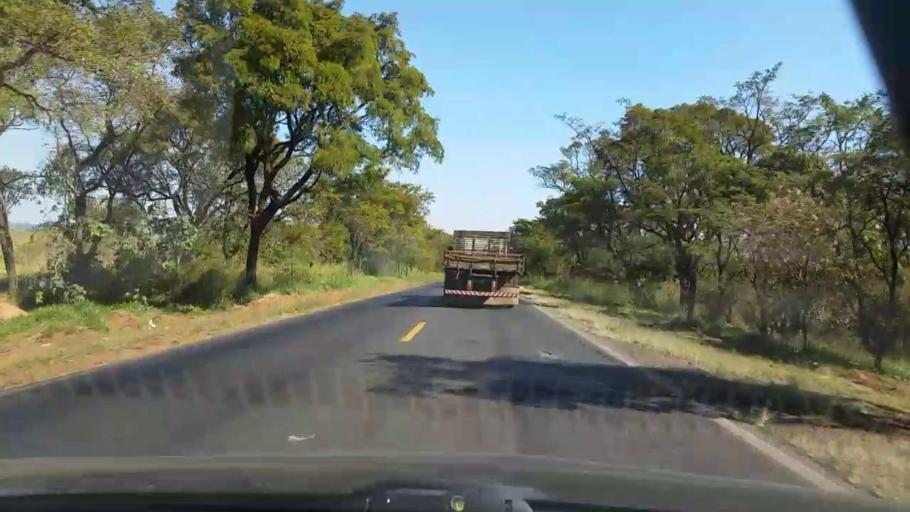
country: BR
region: Sao Paulo
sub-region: Sao Manuel
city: Sao Manuel
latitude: -22.7936
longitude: -48.6572
